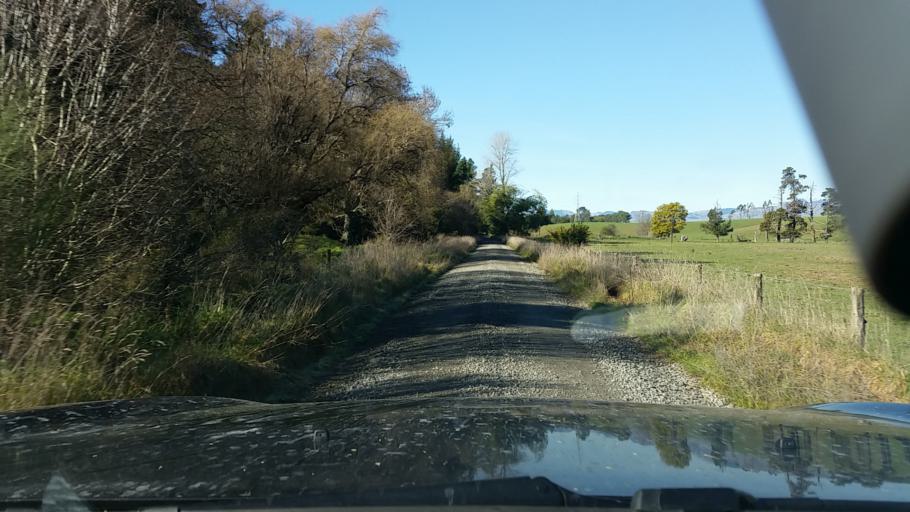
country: NZ
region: Marlborough
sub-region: Marlborough District
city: Blenheim
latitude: -41.4614
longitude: 173.7891
